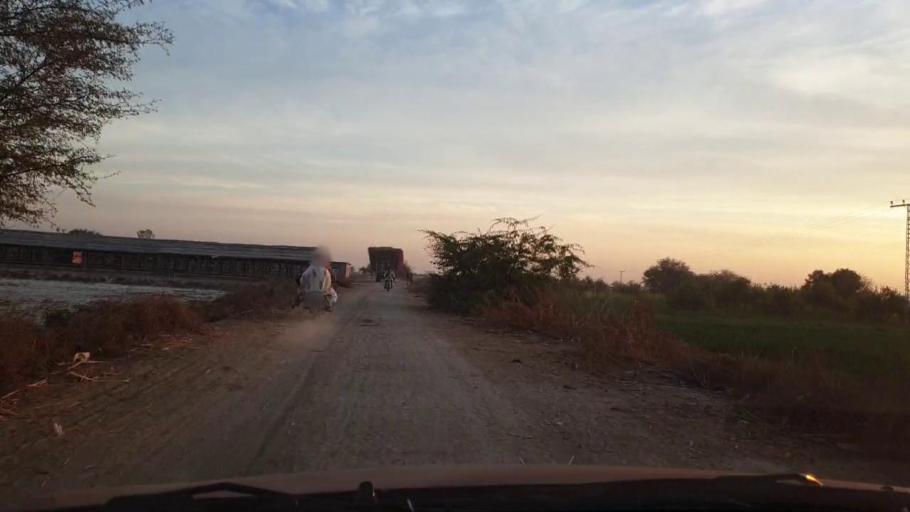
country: PK
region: Sindh
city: Sinjhoro
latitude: 26.1024
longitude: 68.7968
